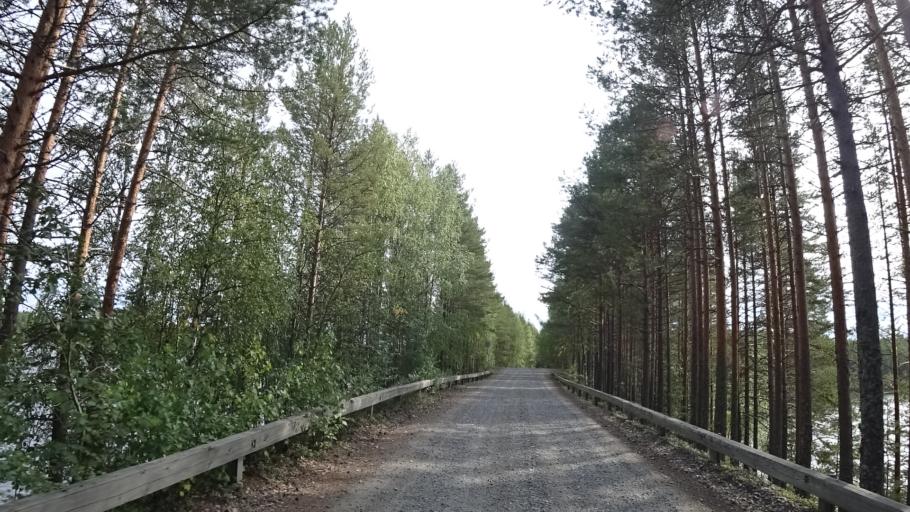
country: FI
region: North Karelia
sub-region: Joensuu
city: Ilomantsi
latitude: 62.6162
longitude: 31.1962
